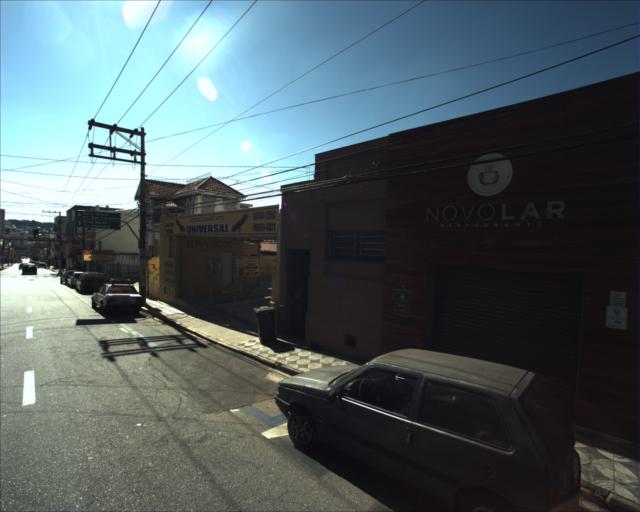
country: BR
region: Sao Paulo
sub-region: Sorocaba
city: Sorocaba
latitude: -23.5001
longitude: -47.4613
